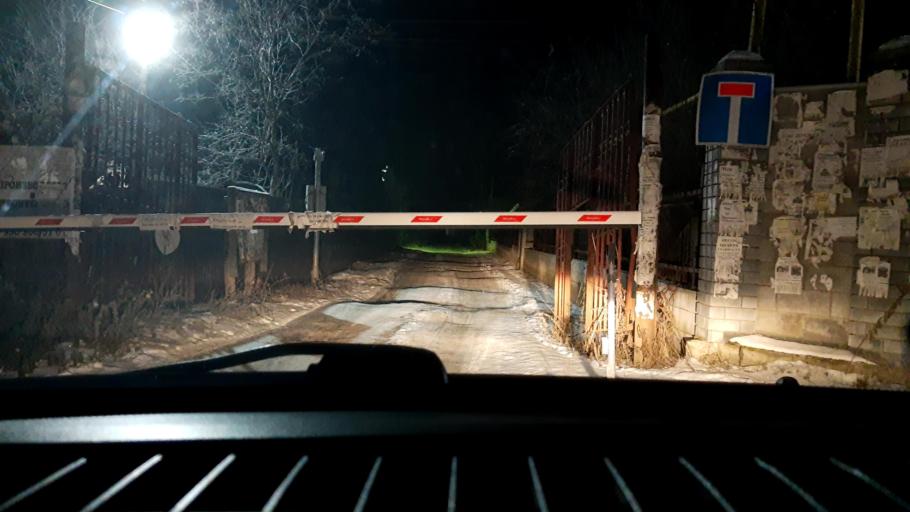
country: RU
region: Nizjnij Novgorod
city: Gorbatovka
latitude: 56.2689
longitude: 43.7832
